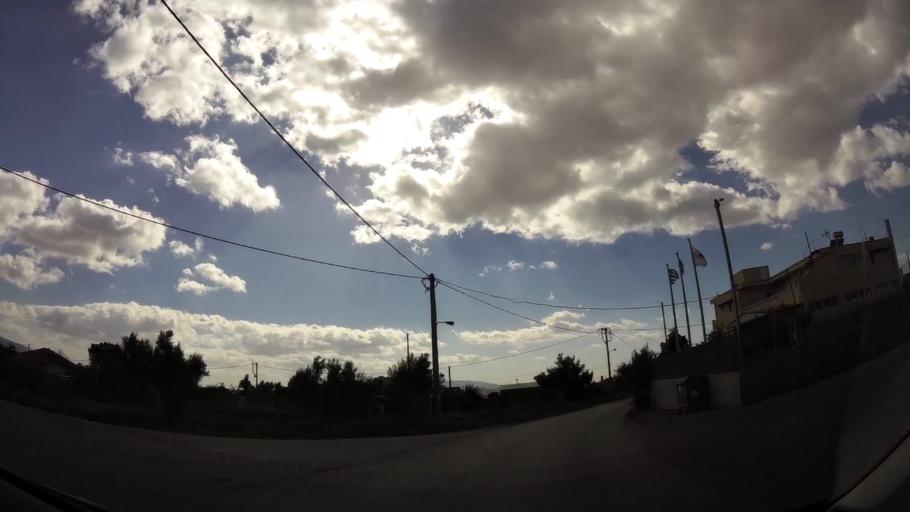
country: GR
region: Attica
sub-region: Nomarchia Anatolikis Attikis
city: Thrakomakedones
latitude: 38.1069
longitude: 23.7606
